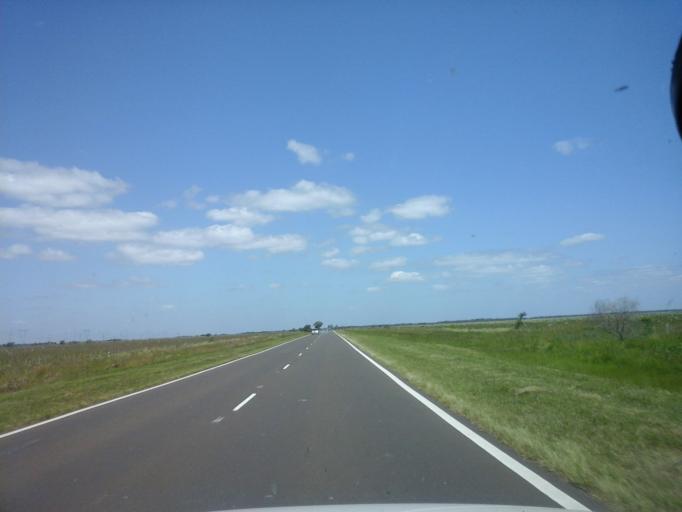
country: PY
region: Neembucu
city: Cerrito
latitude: -27.3732
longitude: -57.8353
